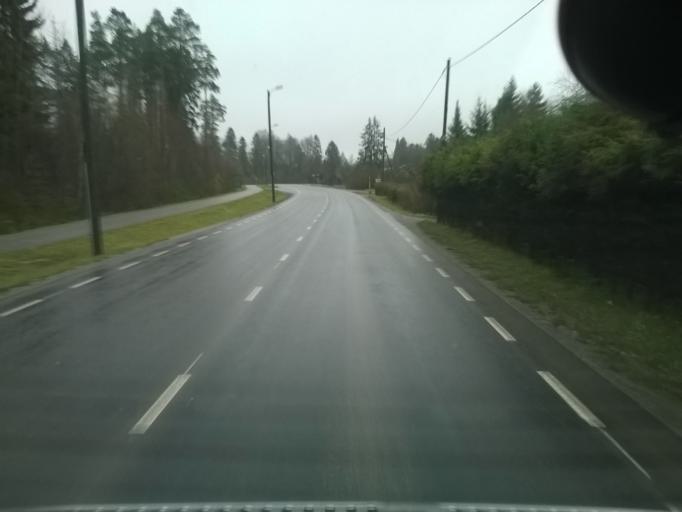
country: EE
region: Harju
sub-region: Saku vald
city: Saku
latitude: 59.2258
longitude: 24.6745
